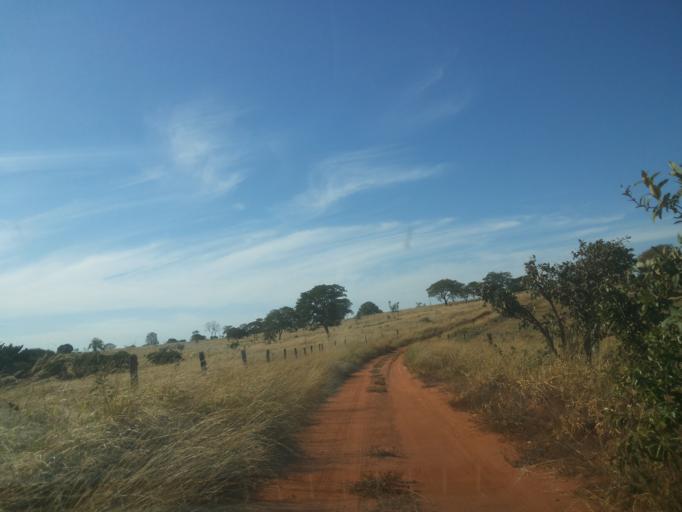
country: BR
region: Minas Gerais
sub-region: Ituiutaba
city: Ituiutaba
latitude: -19.1226
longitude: -49.3926
